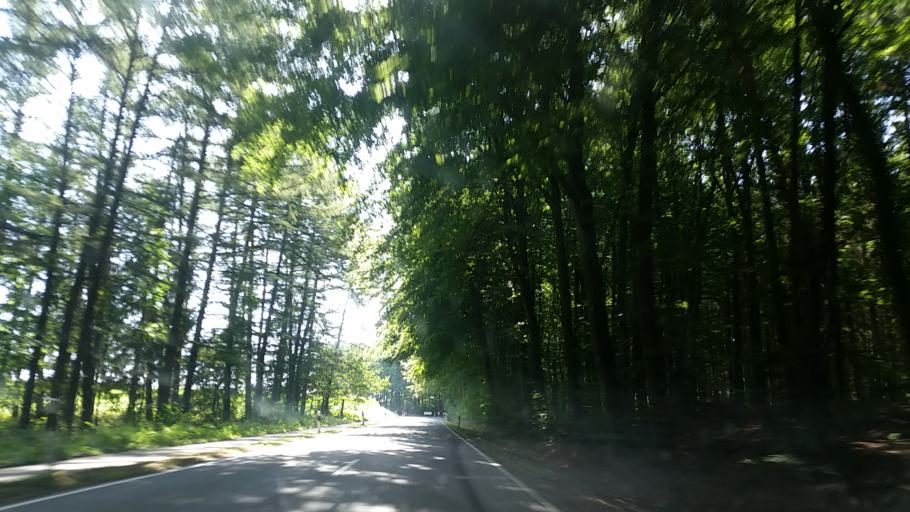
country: DE
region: Lower Saxony
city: Ankum
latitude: 52.5205
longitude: 7.8998
